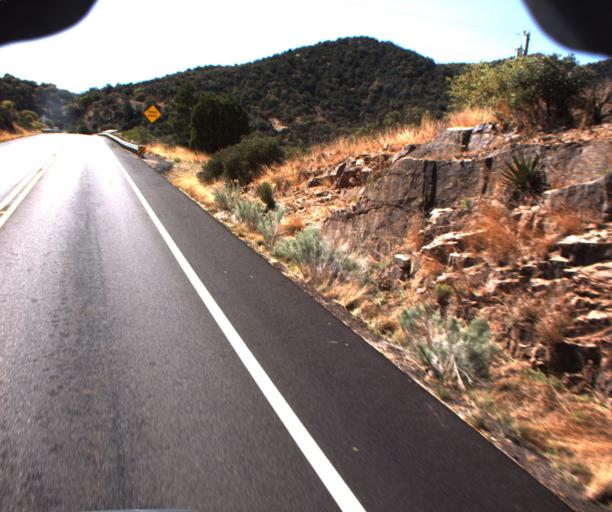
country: US
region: Arizona
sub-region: Cochise County
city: Bisbee
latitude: 31.4622
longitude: -109.9476
